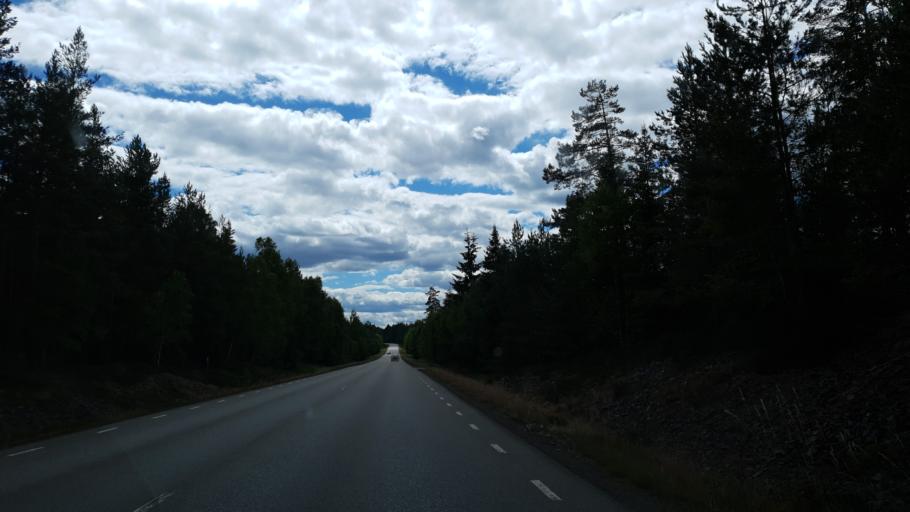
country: SE
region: Kalmar
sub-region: Emmaboda Kommun
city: Emmaboda
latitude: 56.9324
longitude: 15.5788
